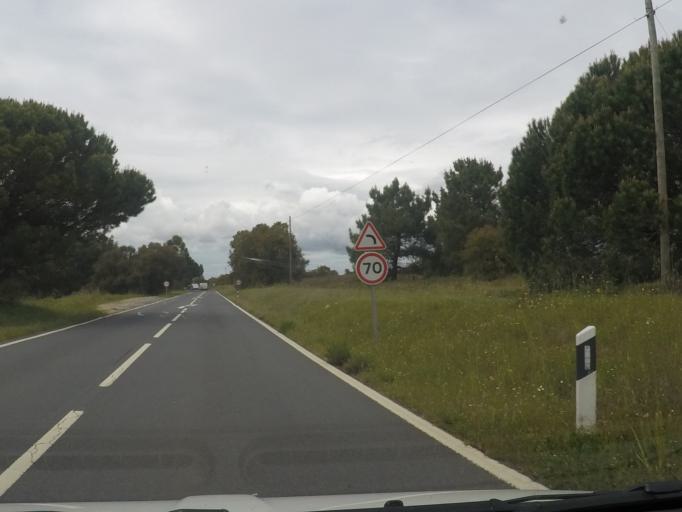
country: PT
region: Setubal
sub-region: Sines
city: Porto Covo
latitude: 37.8778
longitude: -8.7439
